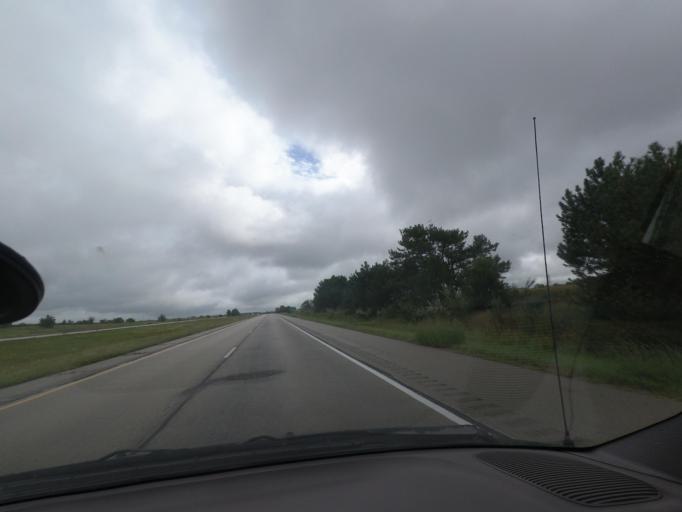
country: US
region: Illinois
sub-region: Piatt County
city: Monticello
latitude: 40.0309
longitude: -88.6211
